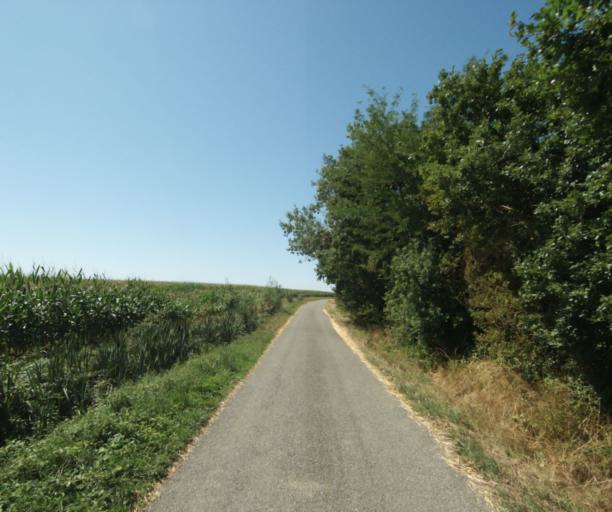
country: FR
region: Midi-Pyrenees
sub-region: Departement de la Haute-Garonne
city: Revel
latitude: 43.4790
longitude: 1.9703
